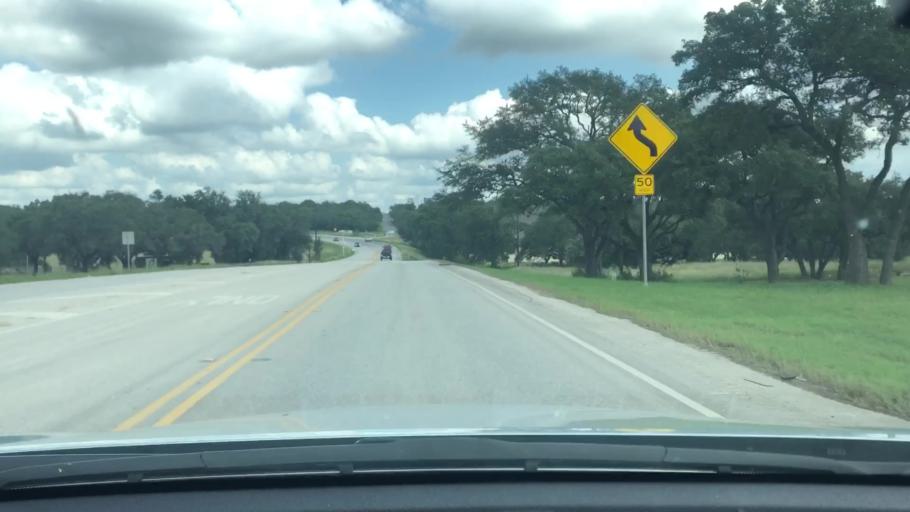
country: US
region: Texas
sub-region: Kendall County
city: Boerne
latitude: 29.7871
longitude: -98.6929
